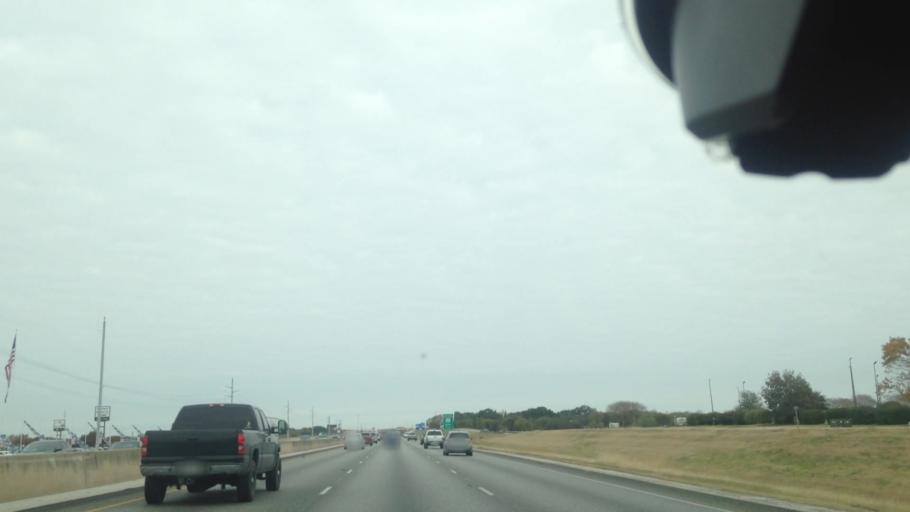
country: US
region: Texas
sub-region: Hays County
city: Kyle
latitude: 29.9332
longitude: -97.8873
